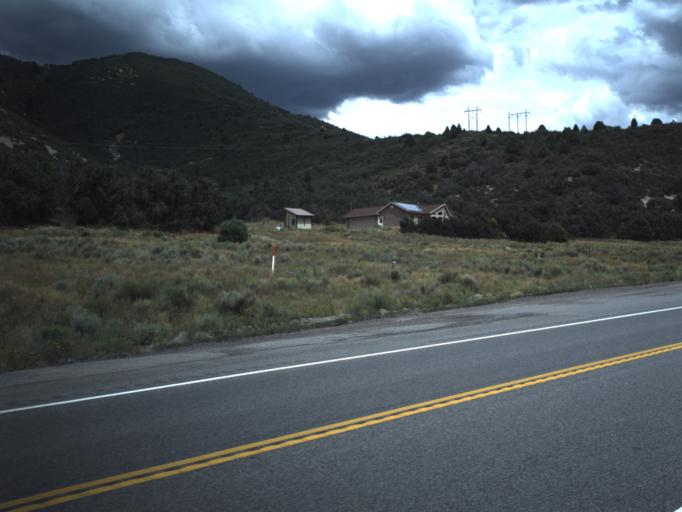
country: US
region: Utah
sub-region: Carbon County
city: Helper
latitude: 39.9361
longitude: -111.1336
